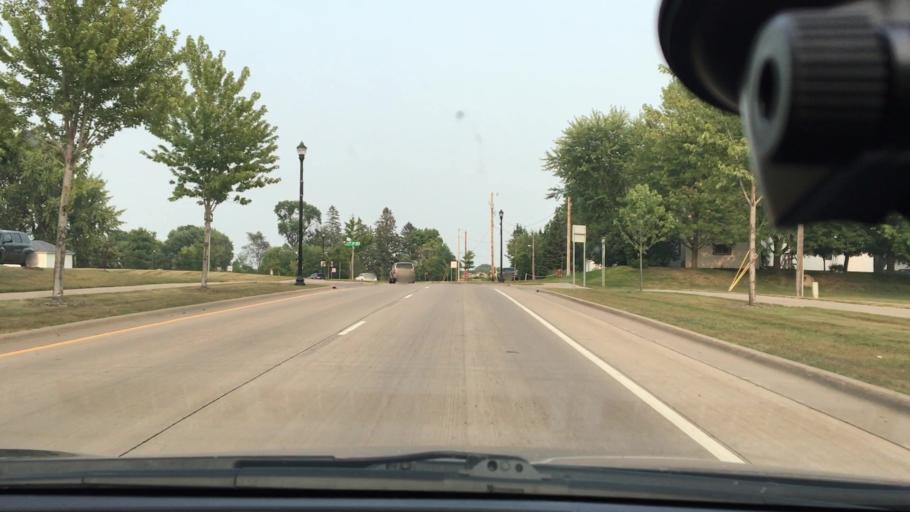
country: US
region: Minnesota
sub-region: Wright County
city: Saint Michael
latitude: 45.2088
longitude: -93.6636
